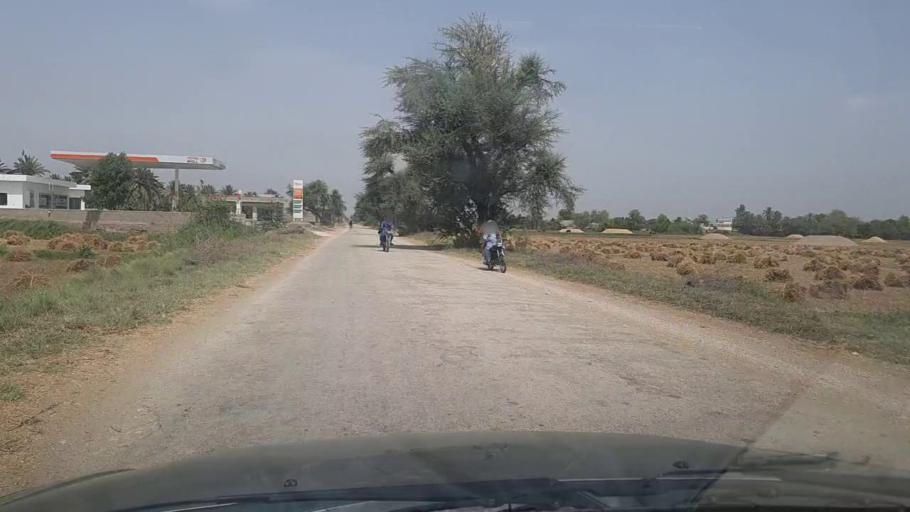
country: PK
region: Sindh
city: Setharja Old
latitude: 27.1928
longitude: 68.4918
